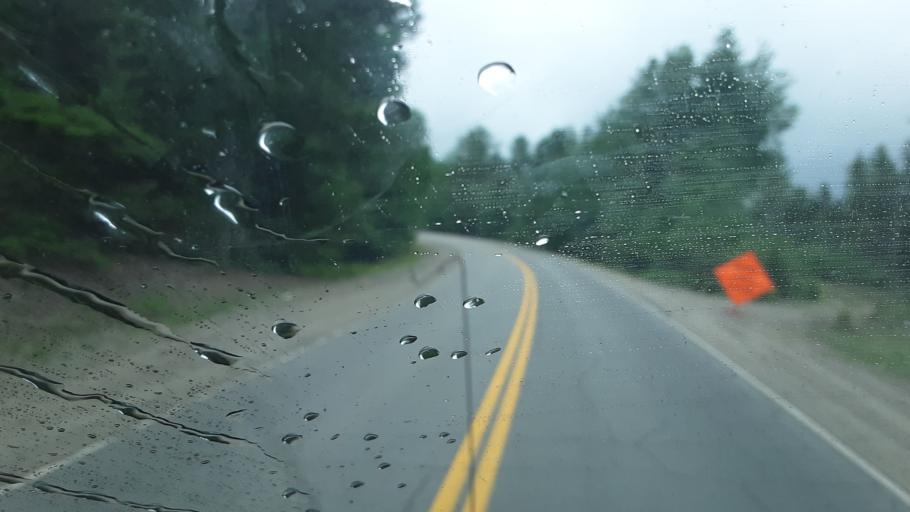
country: US
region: Maine
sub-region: Penobscot County
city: Millinocket
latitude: 45.6939
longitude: -68.7989
